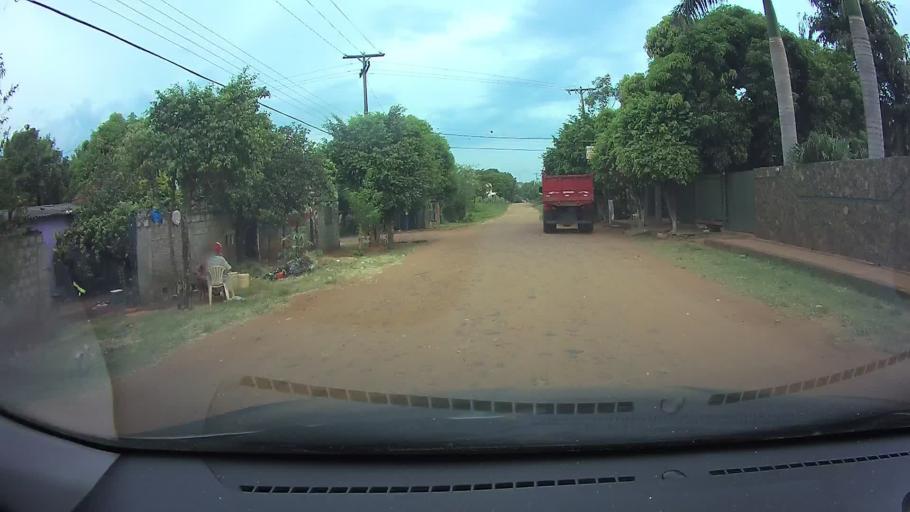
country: PY
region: Central
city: San Lorenzo
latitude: -25.2620
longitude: -57.4635
